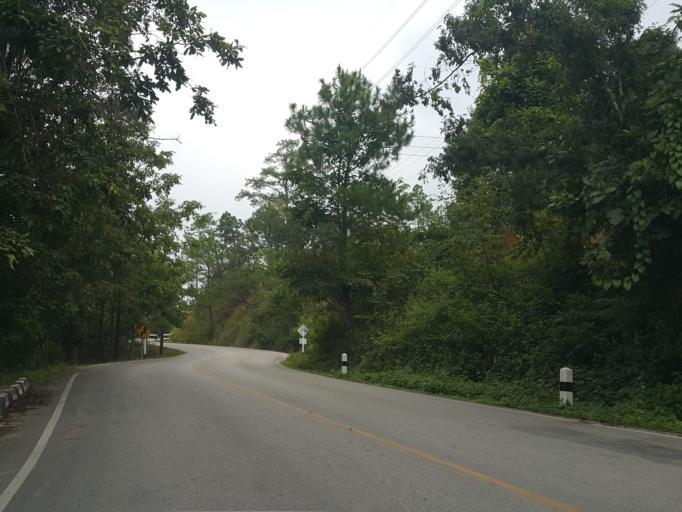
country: TH
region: Mae Hong Son
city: Mae Hi
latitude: 19.2690
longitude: 98.5261
